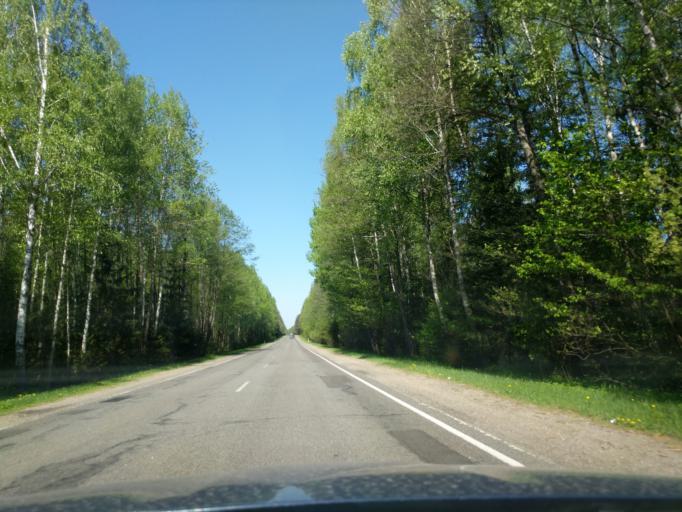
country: BY
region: Minsk
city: Il'ya
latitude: 54.4033
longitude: 27.3224
